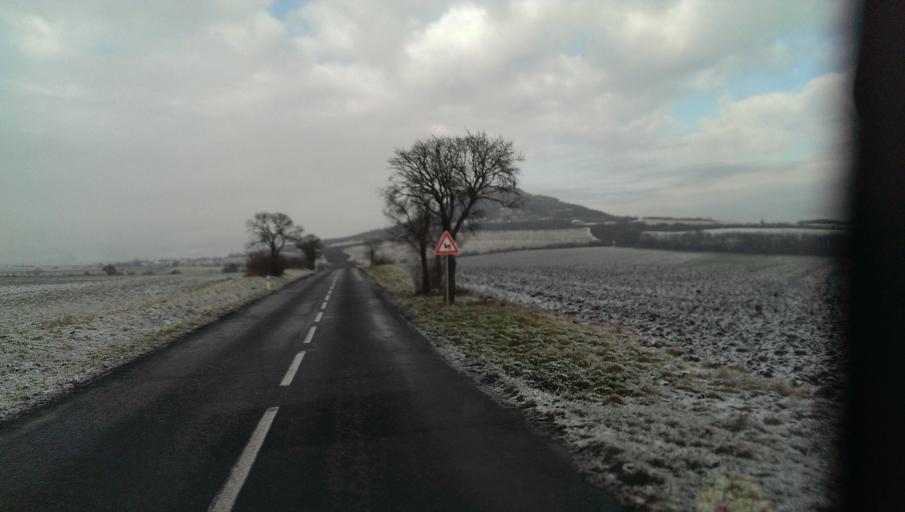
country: CZ
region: Ustecky
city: Libochovice
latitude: 50.4169
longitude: 14.0257
